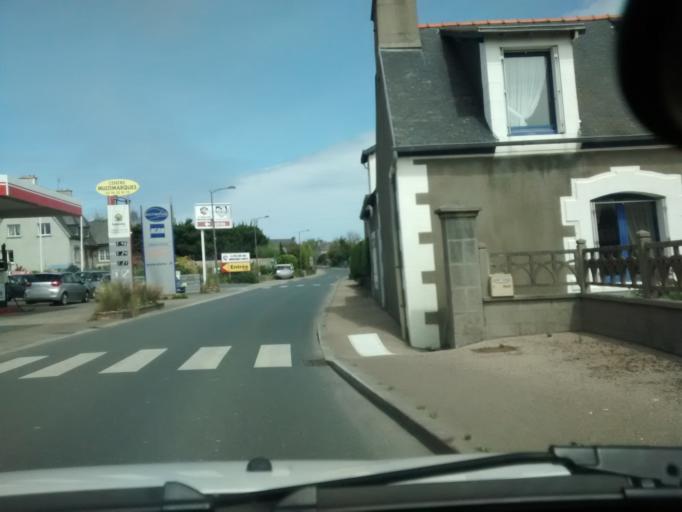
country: FR
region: Brittany
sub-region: Departement des Cotes-d'Armor
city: Ploubazlanec
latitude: 48.7965
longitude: -3.0347
